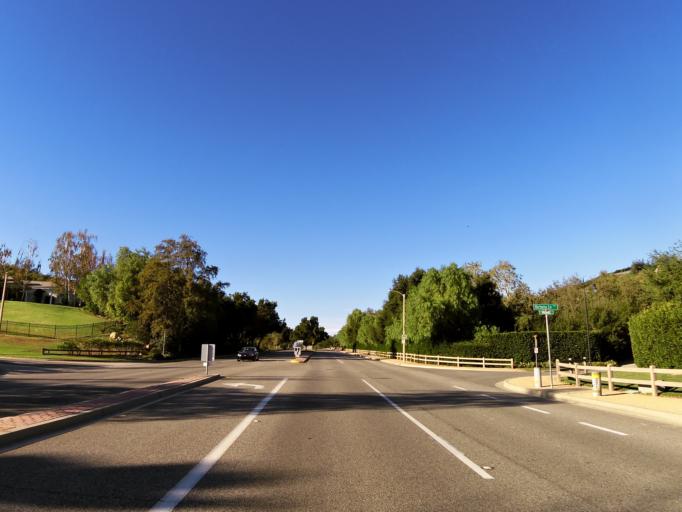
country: US
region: California
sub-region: Ventura County
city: Thousand Oaks
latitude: 34.1989
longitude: -118.8241
